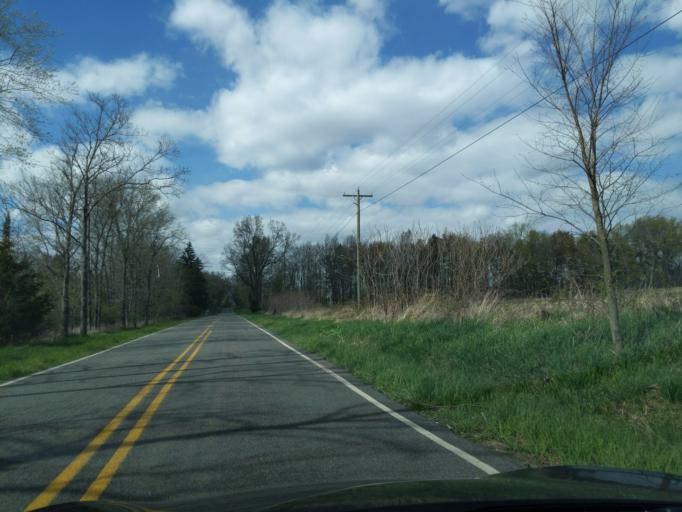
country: US
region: Michigan
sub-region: Ingham County
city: Leslie
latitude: 42.4141
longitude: -84.5415
